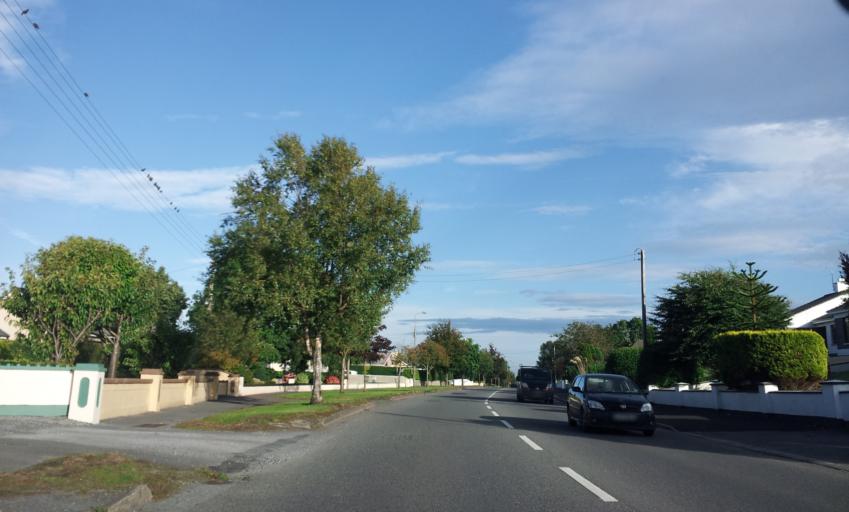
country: IE
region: Munster
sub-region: An Clar
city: Ennis
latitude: 52.8533
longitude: -9.0089
